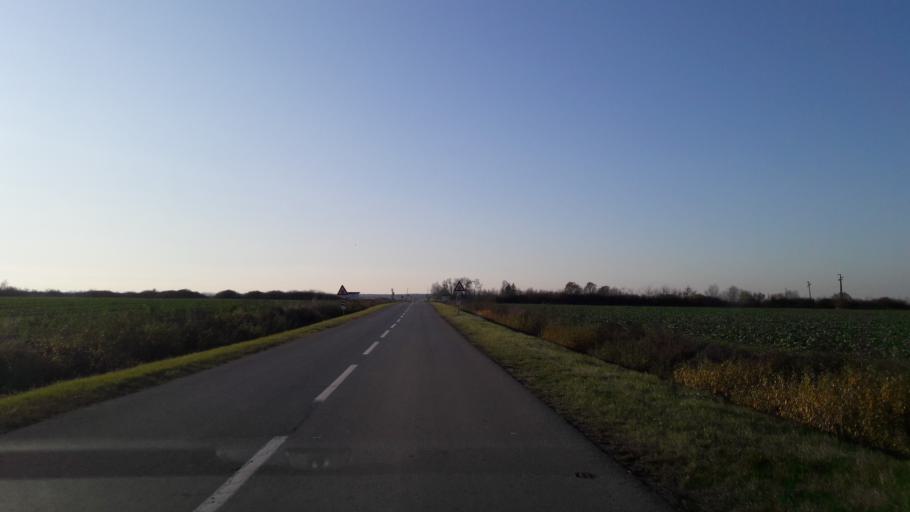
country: HR
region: Osjecko-Baranjska
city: Vuka
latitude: 45.4215
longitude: 18.5280
